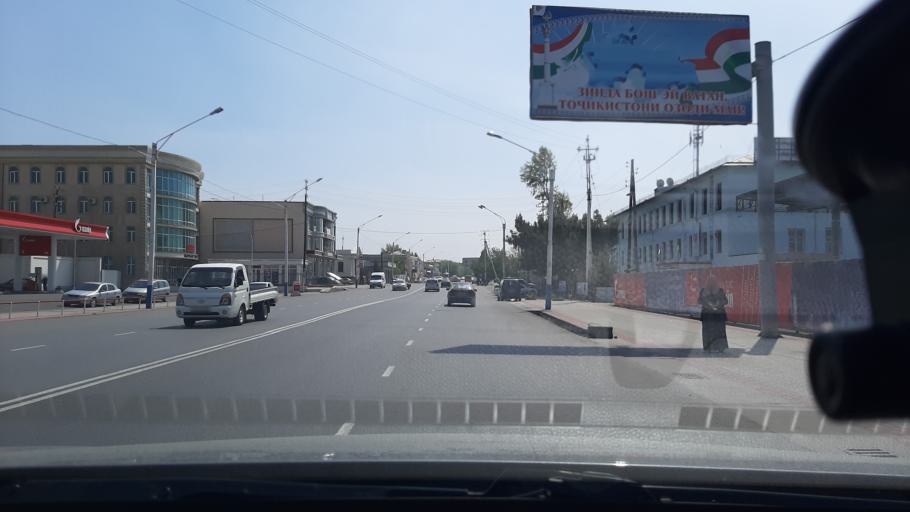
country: TJ
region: Viloyati Sughd
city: Khujand
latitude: 40.2917
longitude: 69.6404
